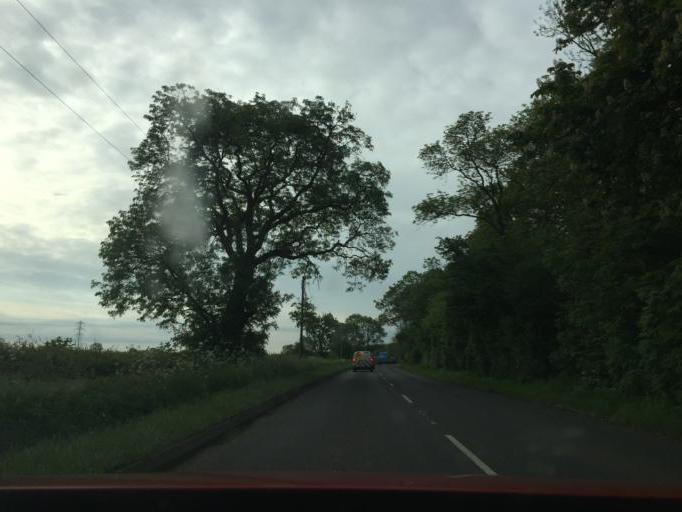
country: GB
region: England
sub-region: Leicestershire
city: Sapcote
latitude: 52.4639
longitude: -1.2986
